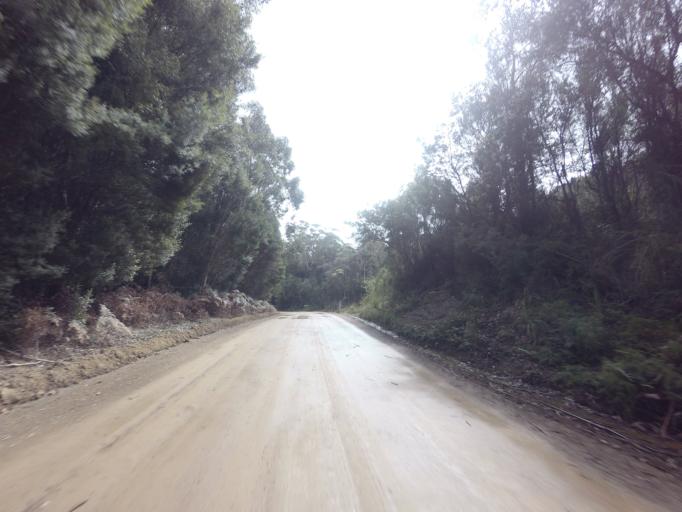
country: AU
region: Tasmania
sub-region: Huon Valley
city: Geeveston
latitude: -43.4068
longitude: 146.8688
